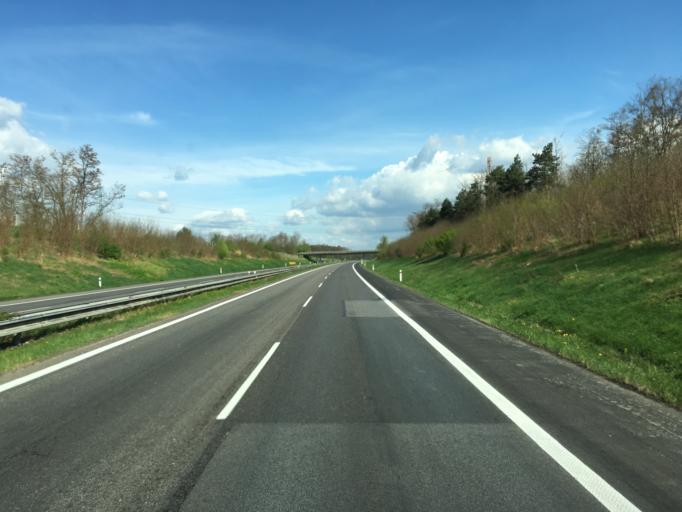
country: SK
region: Bratislavsky
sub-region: Okres Malacky
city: Malacky
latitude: 48.5353
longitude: 17.0162
